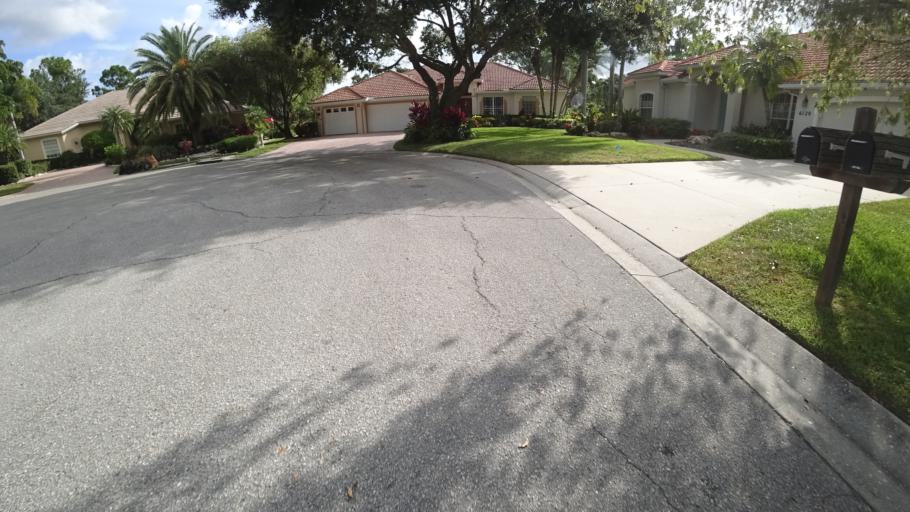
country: US
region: Florida
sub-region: Sarasota County
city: Desoto Lakes
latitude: 27.4133
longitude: -82.4830
